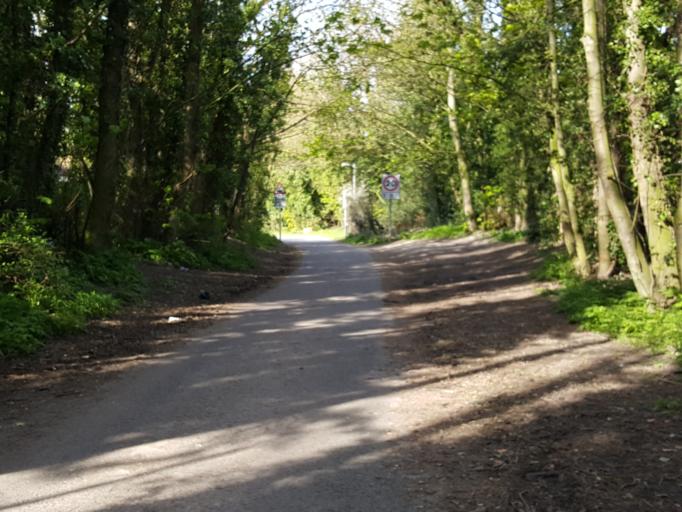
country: GB
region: England
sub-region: East Riding of Yorkshire
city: Welton
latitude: 53.7343
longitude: -0.5428
